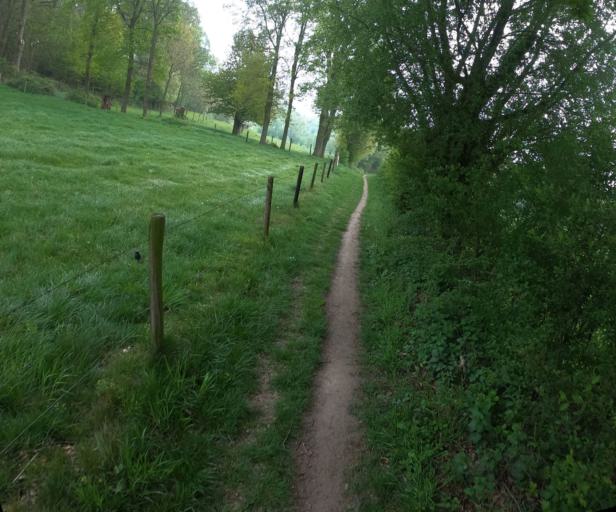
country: BE
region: Flanders
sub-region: Provincie Vlaams-Brabant
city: Gooik
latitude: 50.7811
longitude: 4.1050
